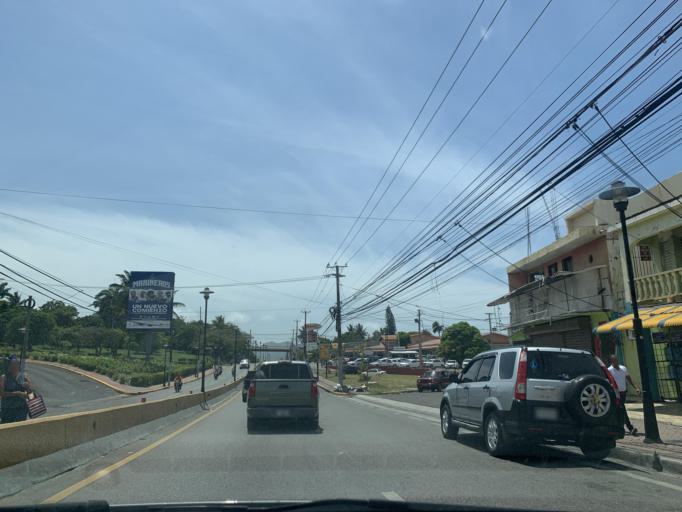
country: DO
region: Puerto Plata
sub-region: Puerto Plata
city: Puerto Plata
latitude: 19.7866
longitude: -70.6898
